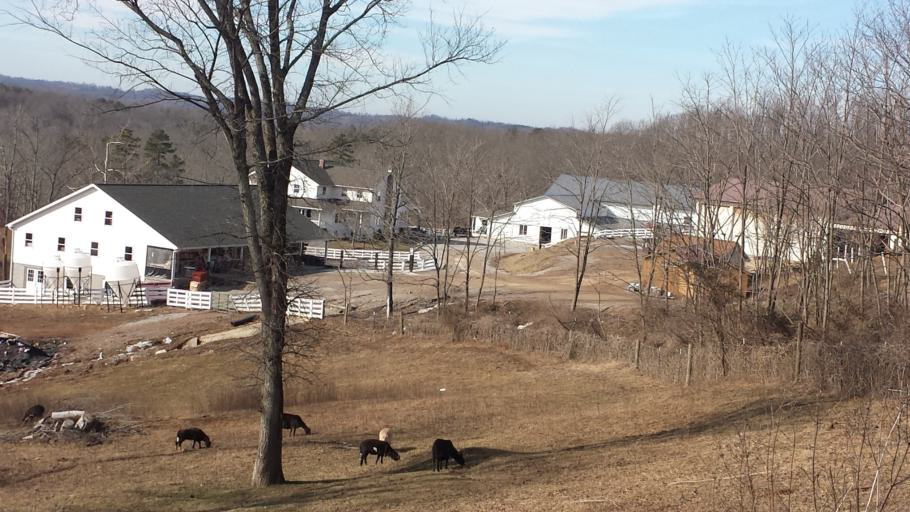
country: US
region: Ohio
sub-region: Gallia County
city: Gallipolis
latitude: 38.7354
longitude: -82.3435
